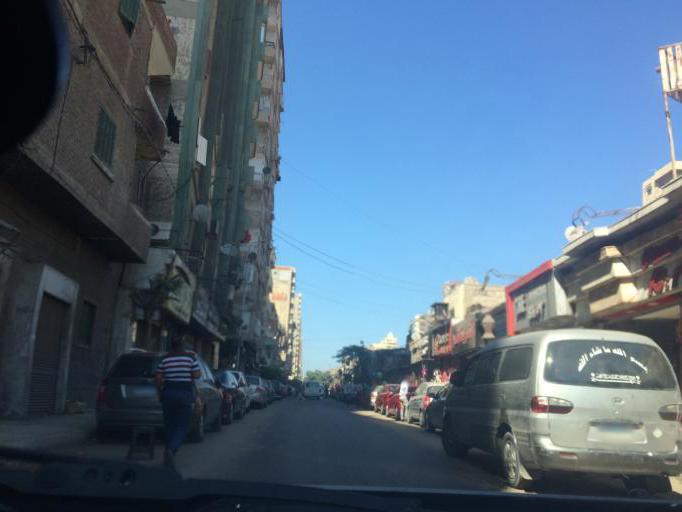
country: EG
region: Alexandria
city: Alexandria
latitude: 31.2515
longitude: 29.9845
